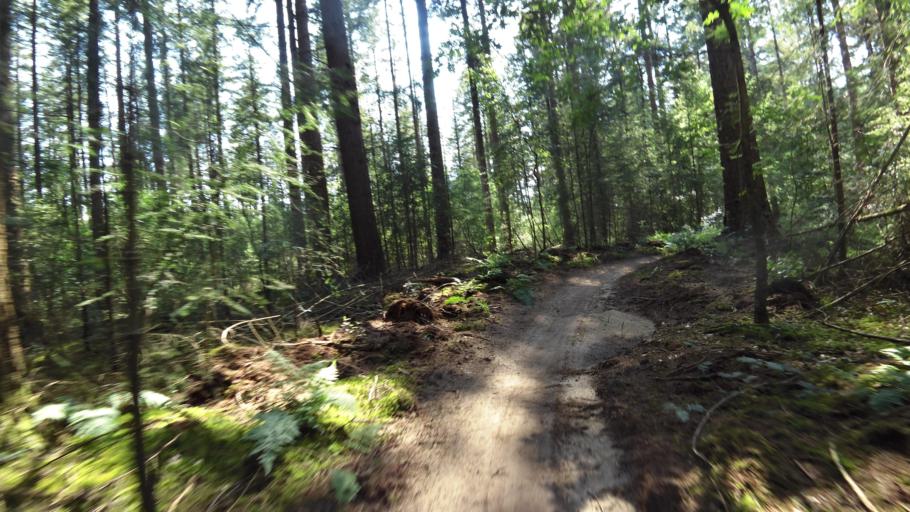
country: NL
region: Gelderland
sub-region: Gemeente Renkum
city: Oosterbeek
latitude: 52.0248
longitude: 5.8427
